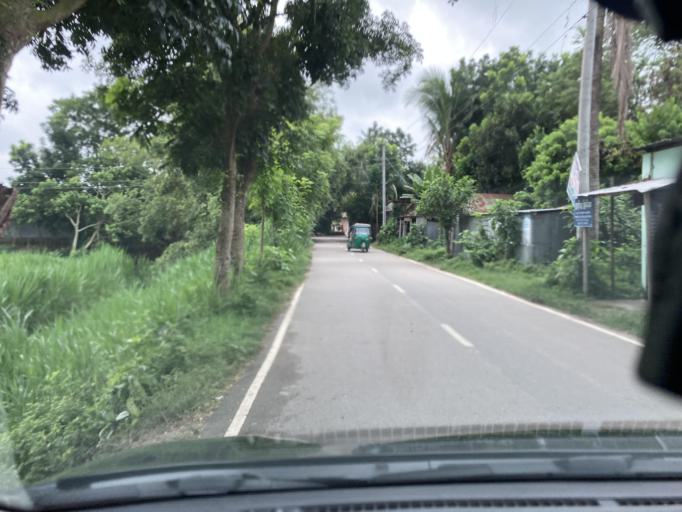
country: BD
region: Dhaka
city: Dohar
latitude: 23.7683
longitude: 90.1970
